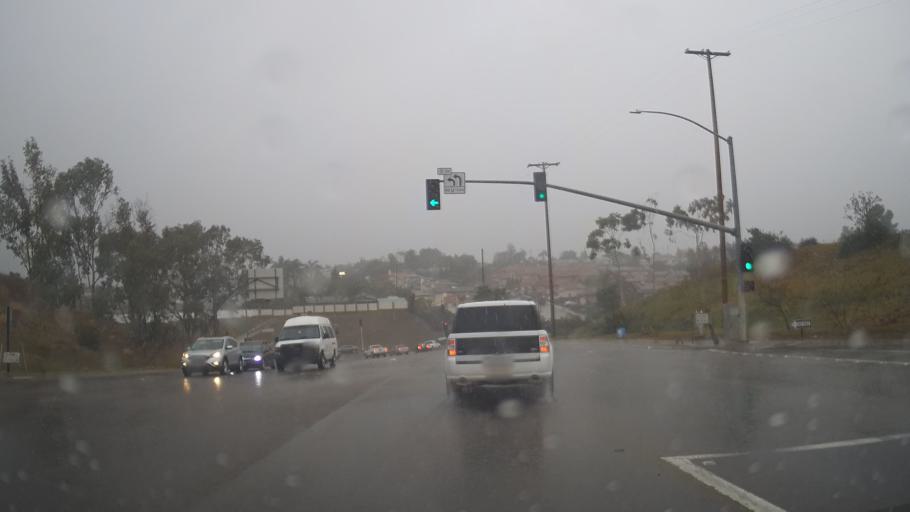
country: US
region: California
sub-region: San Diego County
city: Bonita
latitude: 32.6647
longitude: -117.0573
